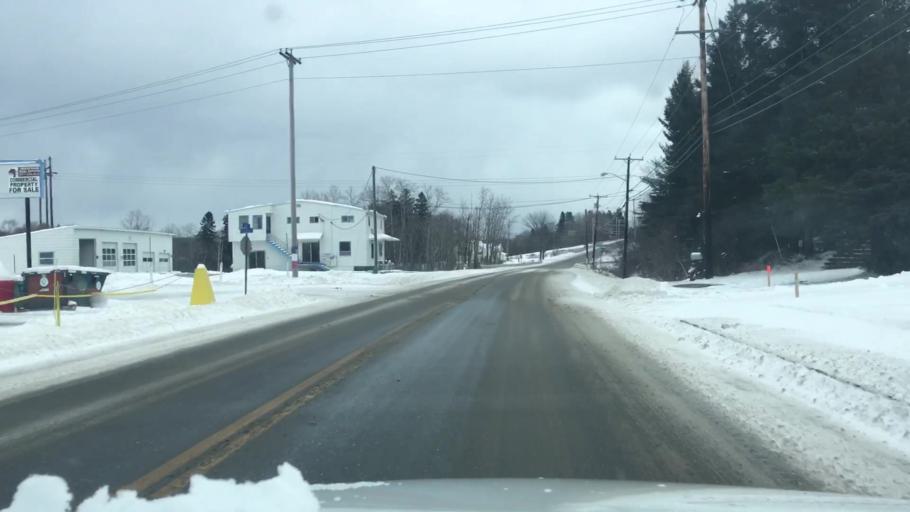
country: US
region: Maine
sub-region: Aroostook County
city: Madawaska
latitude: 47.3528
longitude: -68.2995
